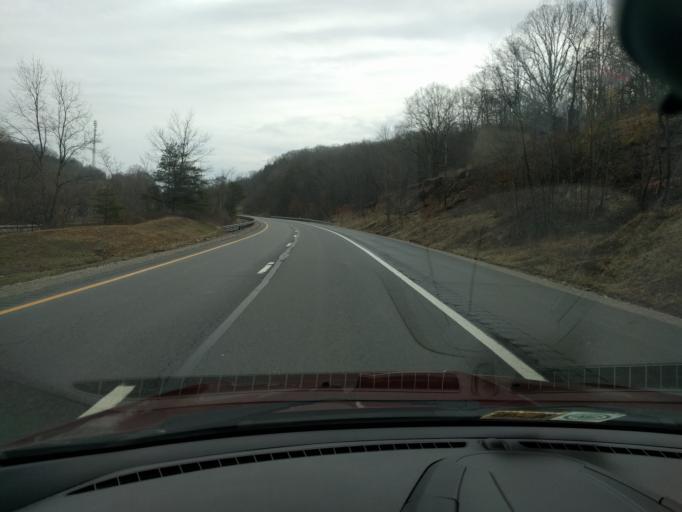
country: US
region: West Virginia
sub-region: Jackson County
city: Ravenswood
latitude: 38.9952
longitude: -81.6580
